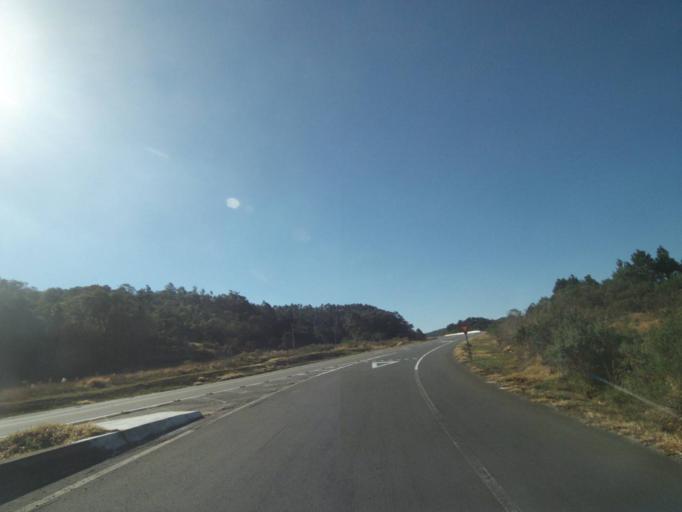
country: BR
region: Parana
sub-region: Tibagi
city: Tibagi
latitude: -24.8142
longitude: -50.4854
